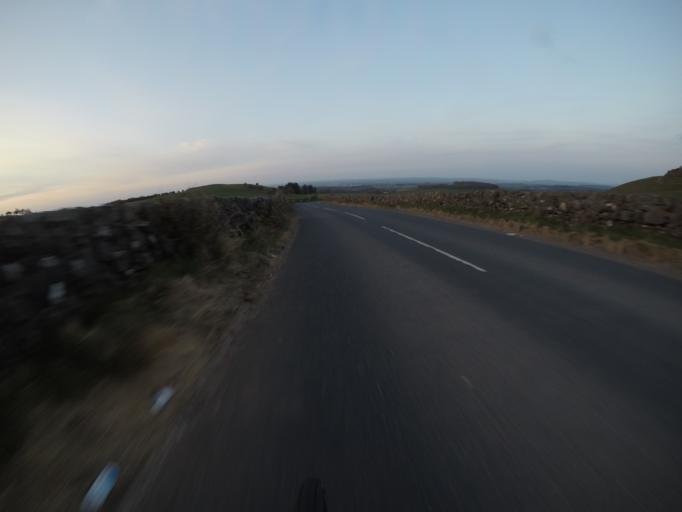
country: GB
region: Scotland
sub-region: South Ayrshire
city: Dundonald
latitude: 55.5619
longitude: -4.6067
